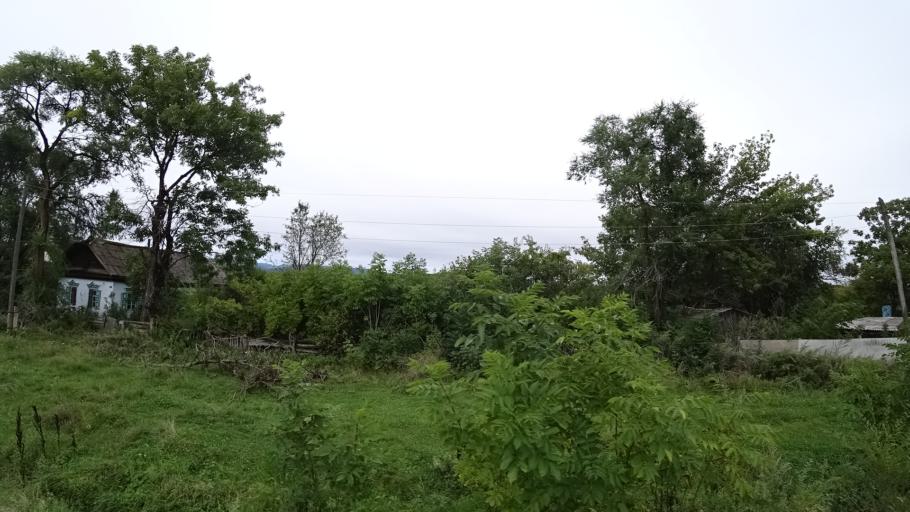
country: RU
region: Primorskiy
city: Monastyrishche
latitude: 44.0835
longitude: 132.5875
